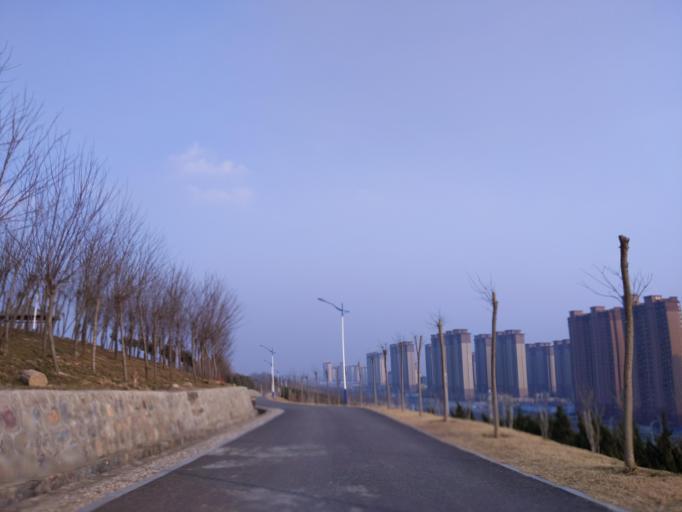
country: CN
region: Henan Sheng
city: Puyang
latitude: 35.8193
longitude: 115.0166
